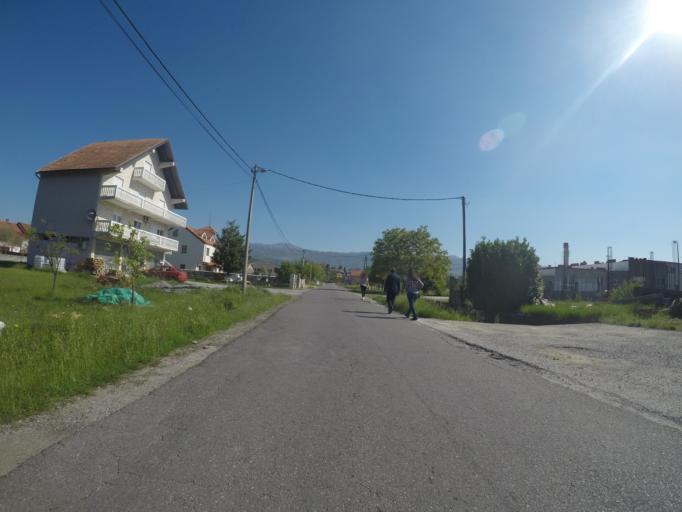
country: ME
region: Danilovgrad
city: Danilovgrad
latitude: 42.5448
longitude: 19.0981
